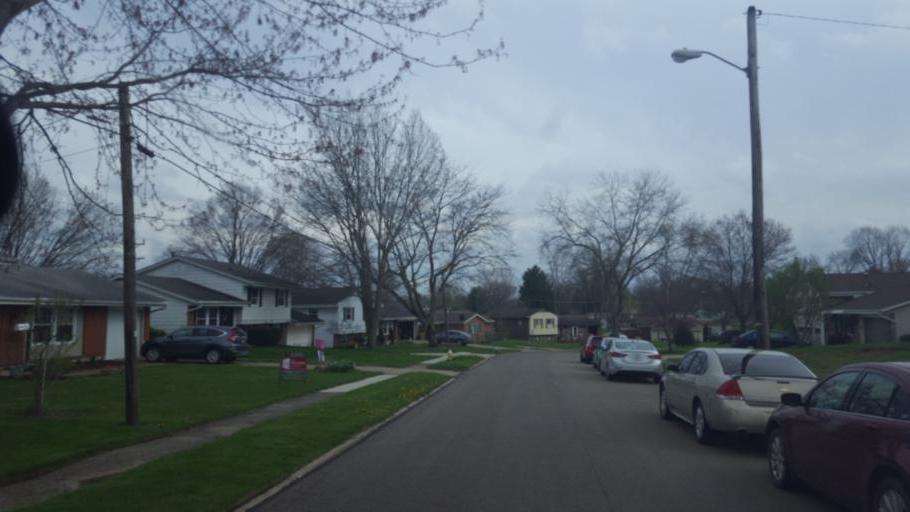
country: US
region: Ohio
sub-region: Richland County
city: Lexington
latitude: 40.6868
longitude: -82.5881
